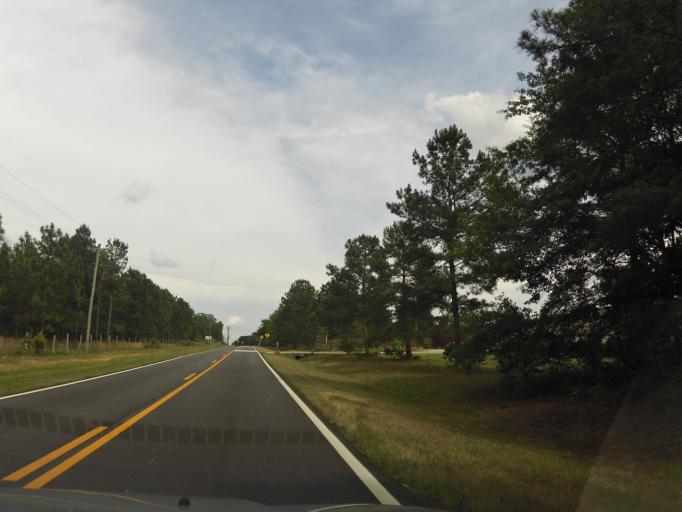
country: US
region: Georgia
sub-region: McDuffie County
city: Thomson
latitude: 33.5236
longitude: -82.4377
